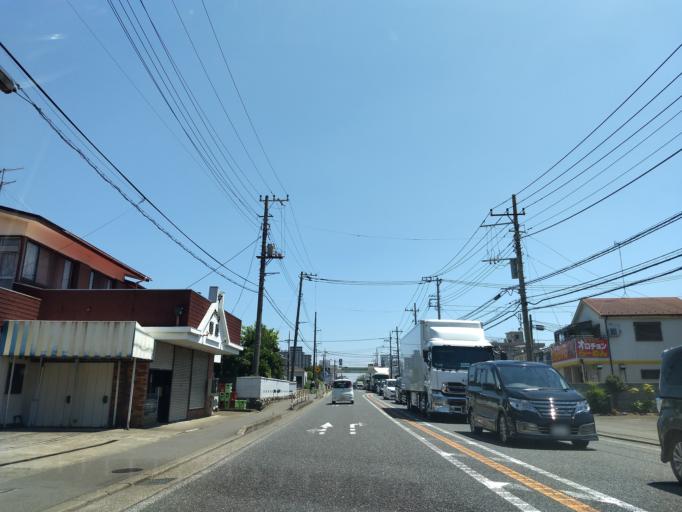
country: JP
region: Kanagawa
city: Isehara
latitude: 35.3939
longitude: 139.2870
